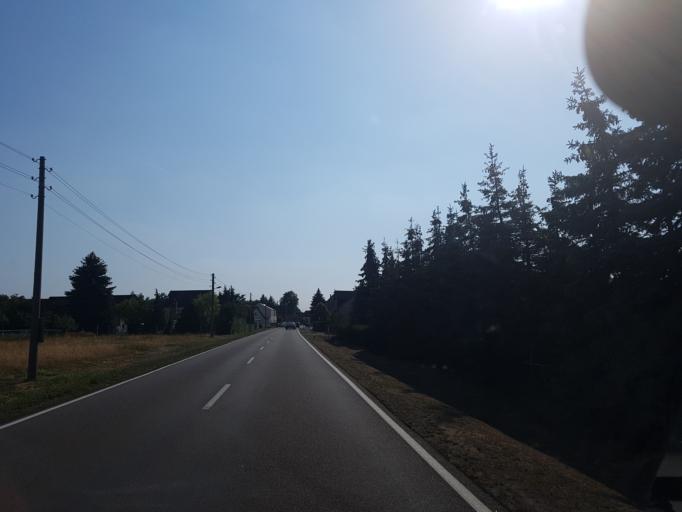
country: DE
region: Saxony-Anhalt
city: Annaburg
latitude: 51.7068
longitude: 13.0206
